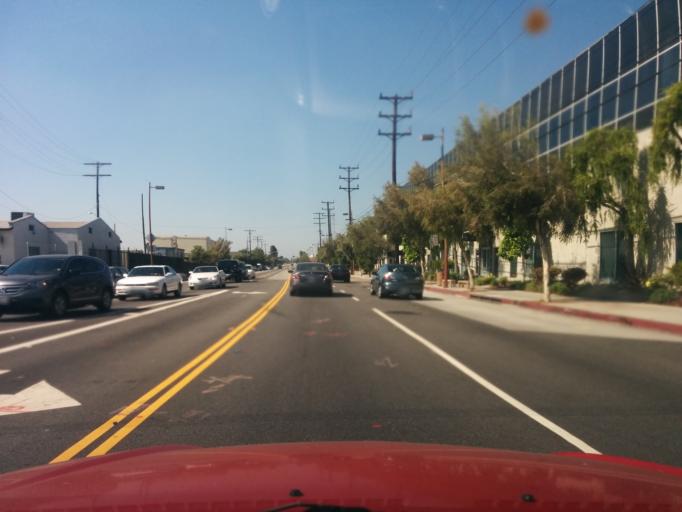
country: US
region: California
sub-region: Los Angeles County
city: North Glendale
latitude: 34.1617
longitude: -118.2824
